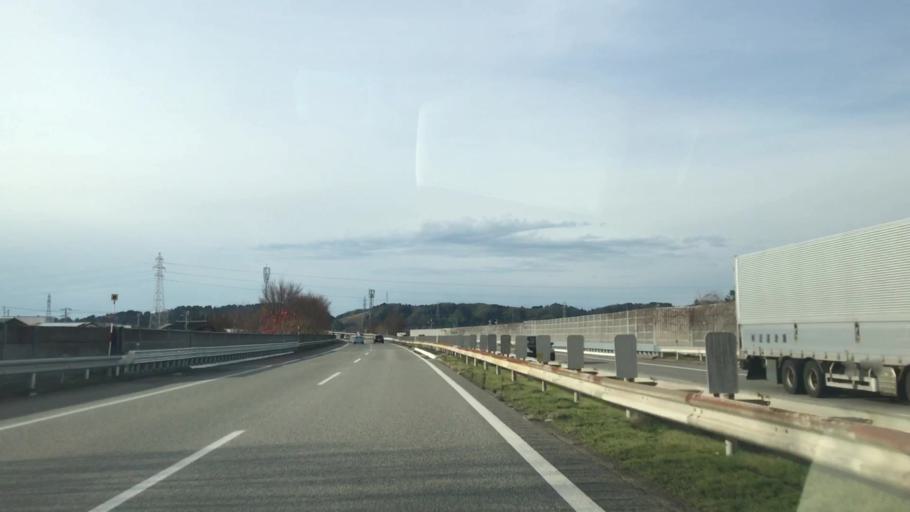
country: JP
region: Toyama
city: Toyama-shi
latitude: 36.6725
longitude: 137.1749
